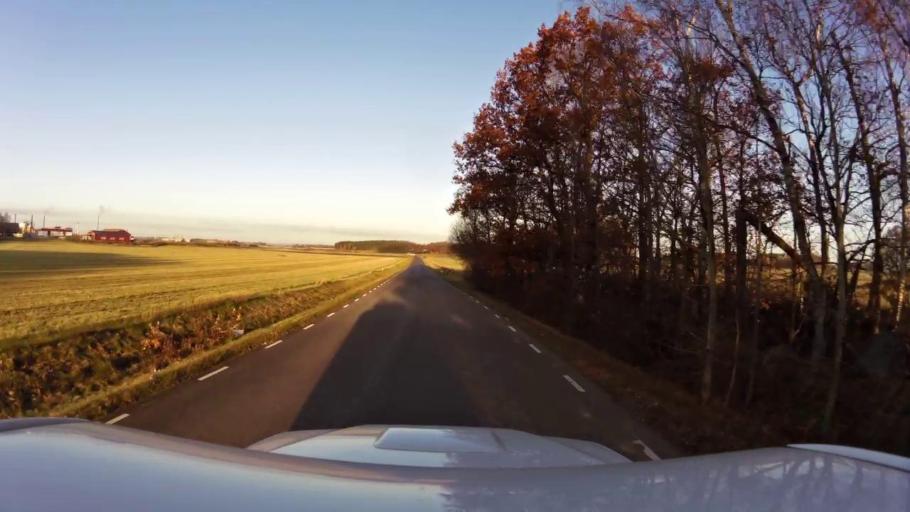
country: SE
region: OEstergoetland
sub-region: Linkopings Kommun
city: Ekangen
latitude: 58.4369
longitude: 15.6799
